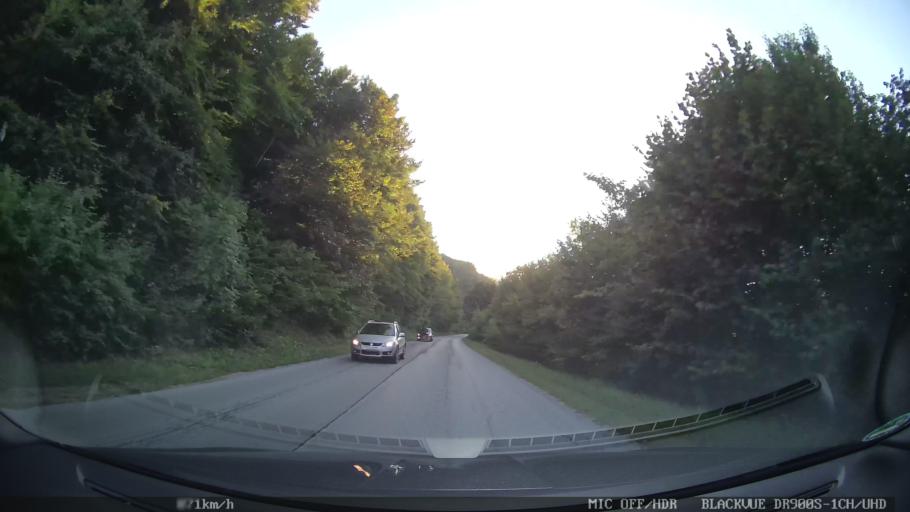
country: HR
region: Karlovacka
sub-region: Grad Ogulin
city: Ogulin
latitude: 45.2691
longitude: 15.1857
